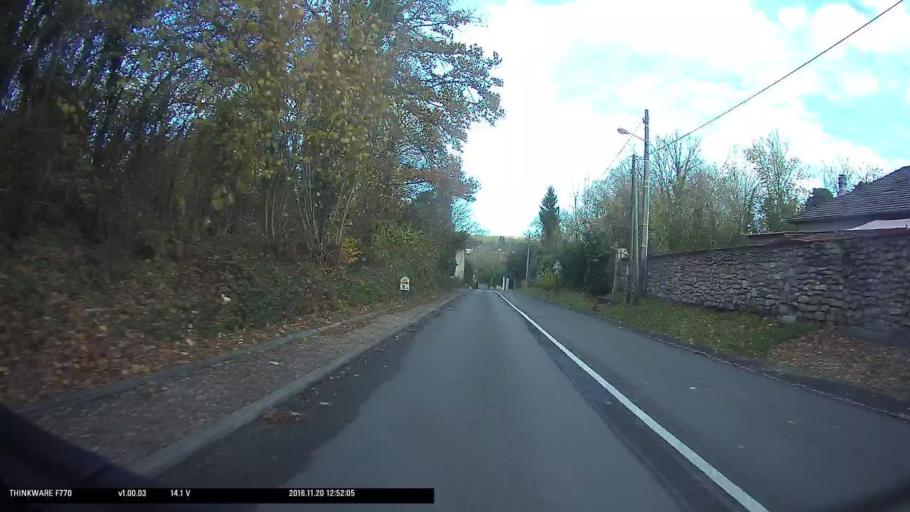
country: FR
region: Ile-de-France
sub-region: Departement du Val-d'Oise
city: Ableiges
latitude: 49.0877
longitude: 1.9808
